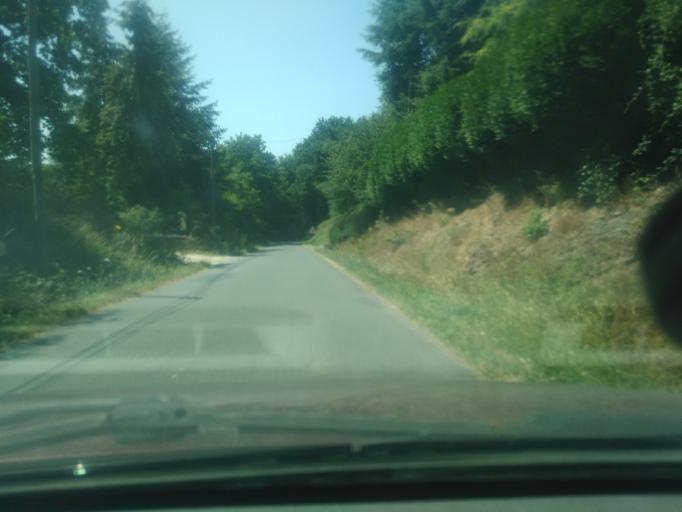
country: FR
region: Pays de la Loire
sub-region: Departement de la Vendee
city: Dompierre-sur-Yon
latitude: 46.7217
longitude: -1.3778
